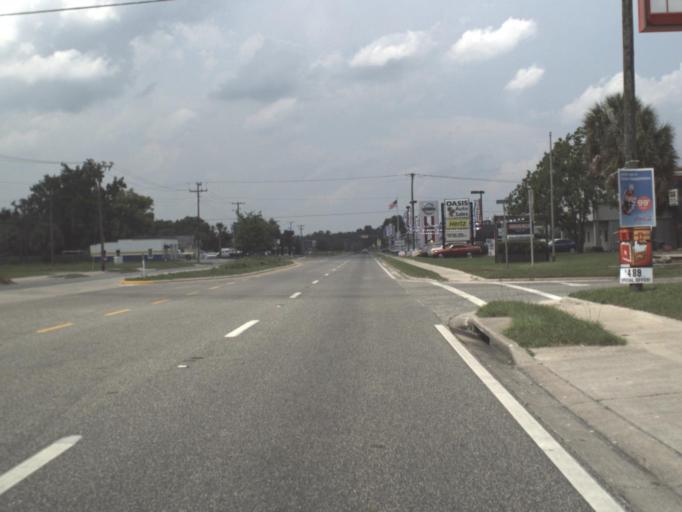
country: US
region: Florida
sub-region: Putnam County
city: Palatka
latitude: 29.6614
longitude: -81.6560
